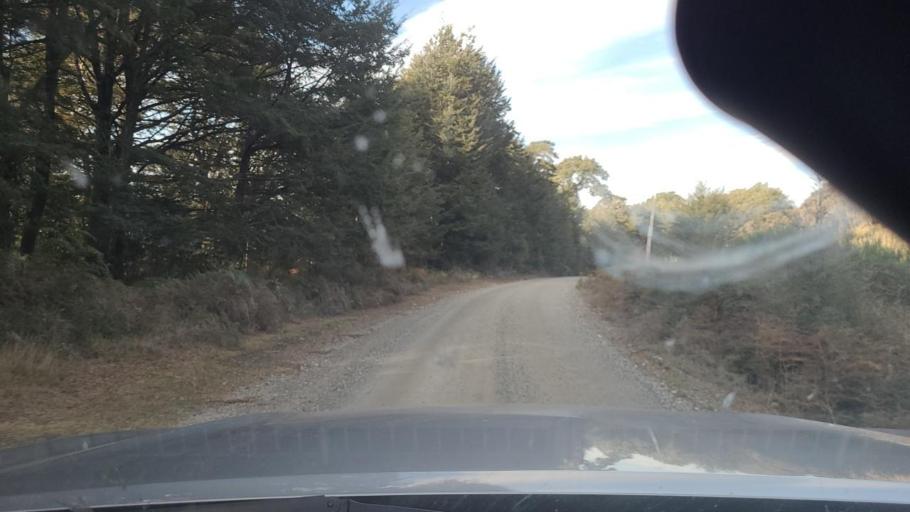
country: NZ
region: Southland
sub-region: Southland District
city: Te Anau
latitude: -45.7958
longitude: 167.6305
